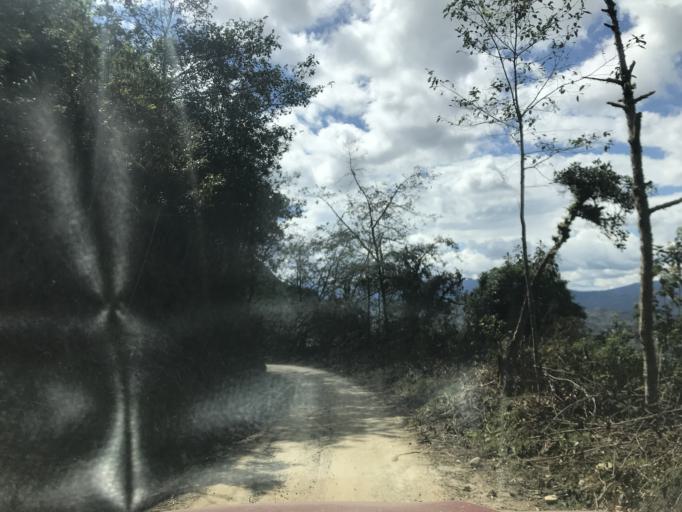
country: PE
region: Cajamarca
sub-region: Provincia de Chota
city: Querocoto
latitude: -6.3458
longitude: -79.0510
